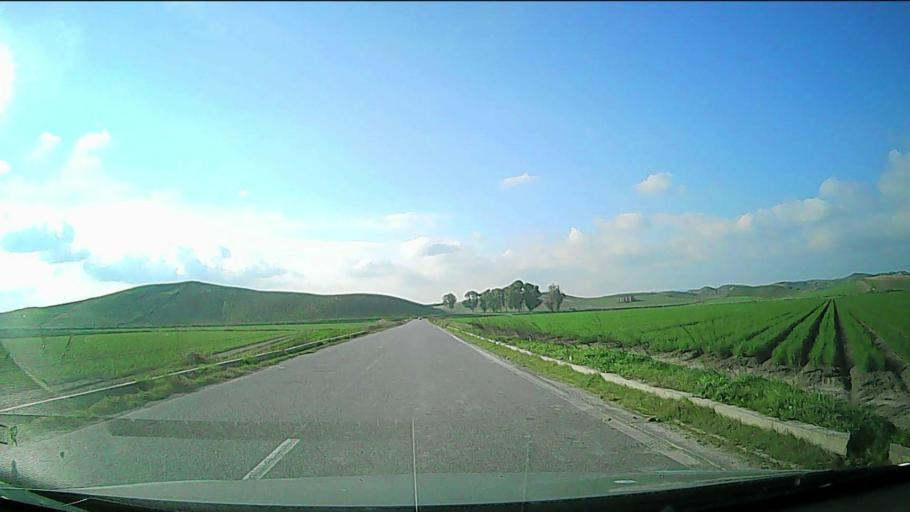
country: IT
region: Calabria
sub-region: Provincia di Crotone
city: Rocca di Neto
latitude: 39.1993
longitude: 17.0658
